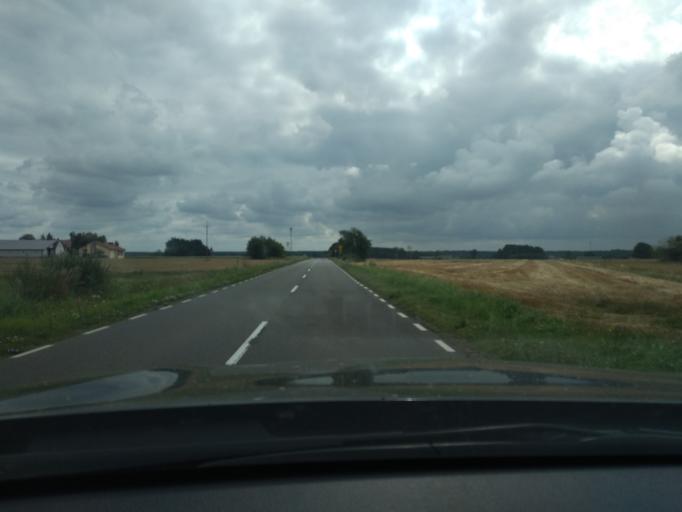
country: PL
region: Masovian Voivodeship
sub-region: Powiat pultuski
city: Obryte
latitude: 52.6548
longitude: 21.2315
